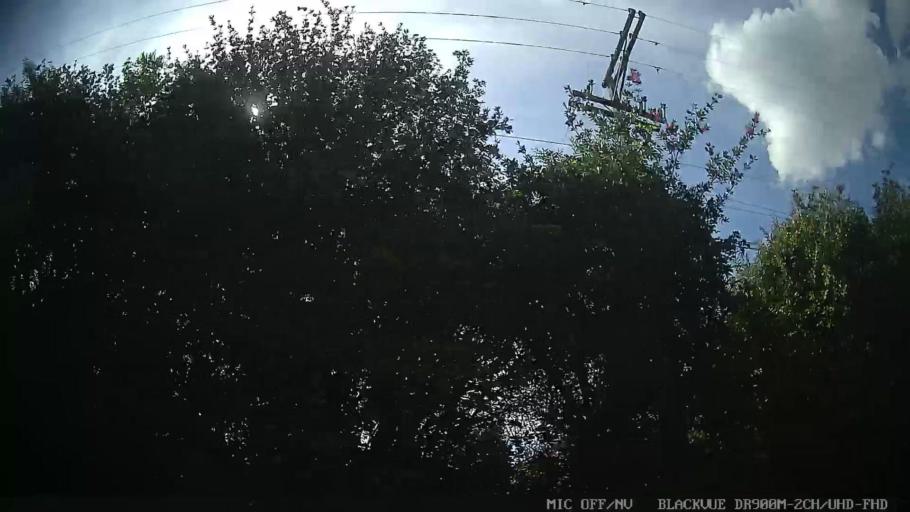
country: BR
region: Sao Paulo
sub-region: Artur Nogueira
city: Artur Nogueira
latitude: -22.6391
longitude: -47.0876
